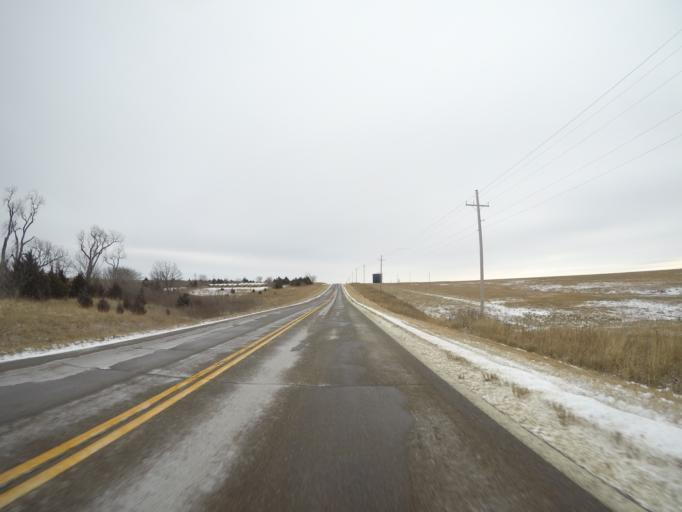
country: US
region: Kansas
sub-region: Wabaunsee County
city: Alma
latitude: 38.8662
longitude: -96.1254
